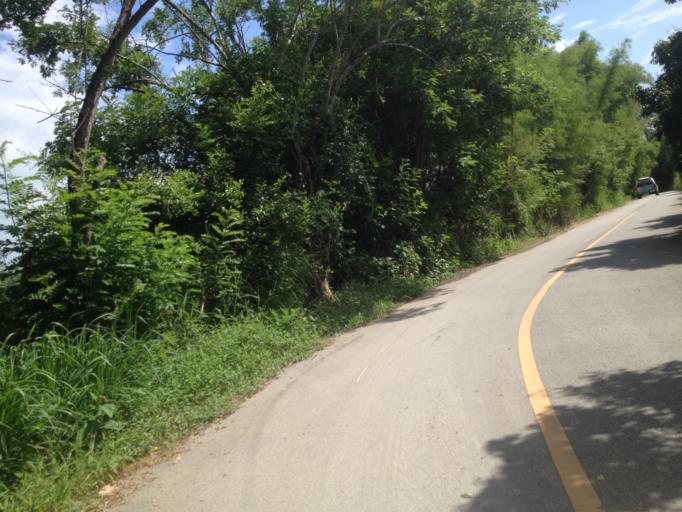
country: TH
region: Chiang Mai
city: Hang Dong
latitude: 18.6795
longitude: 98.8841
